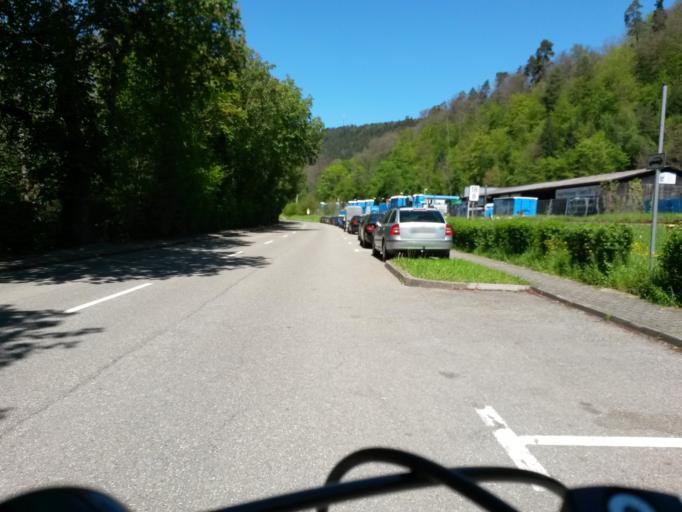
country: DE
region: Baden-Wuerttemberg
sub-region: Karlsruhe Region
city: Bad Liebenzell
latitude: 48.7737
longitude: 8.7341
